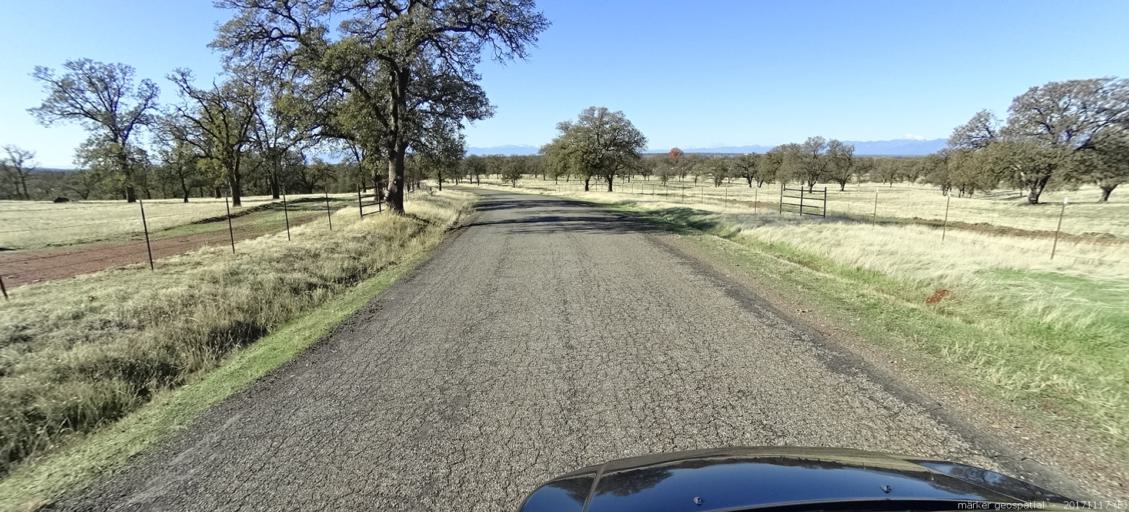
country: US
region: California
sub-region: Shasta County
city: Cottonwood
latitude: 40.4247
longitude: -122.1849
